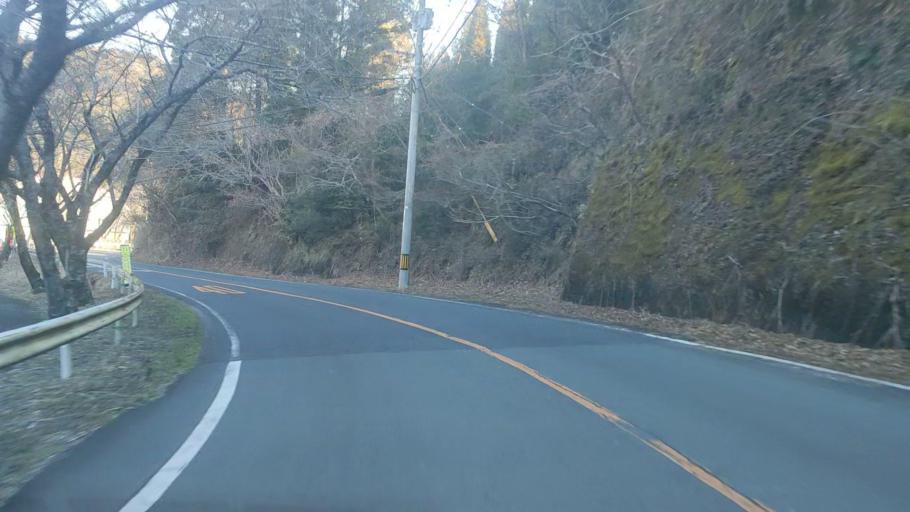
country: JP
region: Oita
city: Saiki
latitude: 32.7646
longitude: 131.7970
